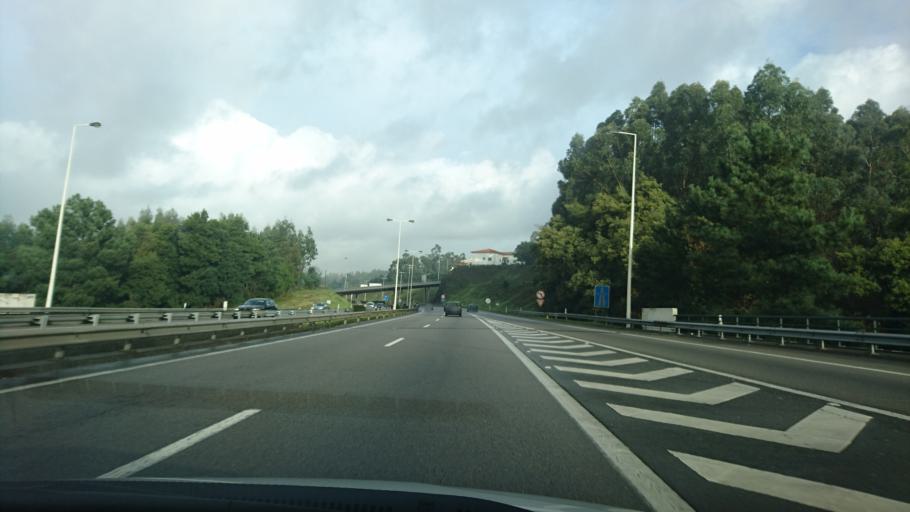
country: PT
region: Porto
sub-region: Gondomar
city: Gondomar
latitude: 41.1500
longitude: -8.5481
